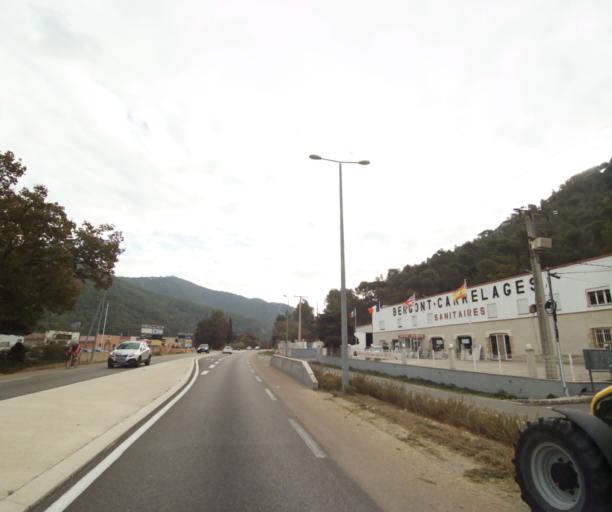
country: FR
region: Provence-Alpes-Cote d'Azur
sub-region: Departement des Bouches-du-Rhone
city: Gemenos
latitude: 43.2769
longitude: 5.6275
